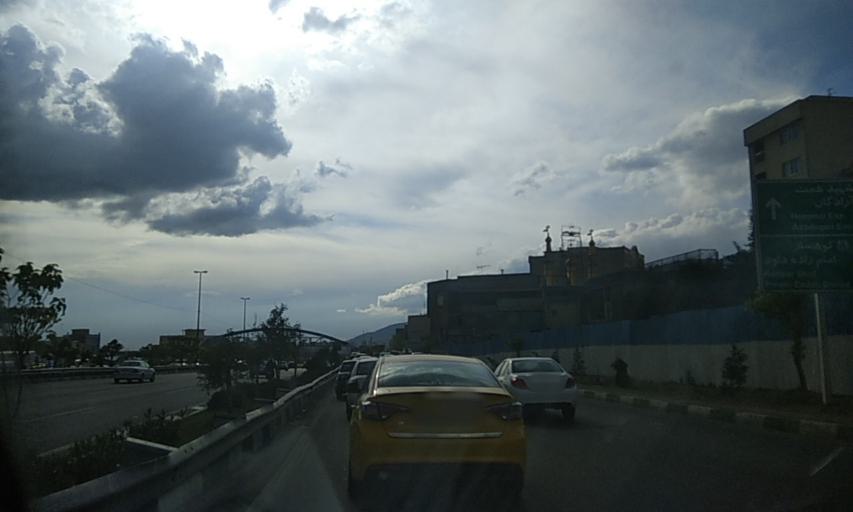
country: IR
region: Tehran
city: Tehran
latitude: 35.7537
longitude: 51.2887
